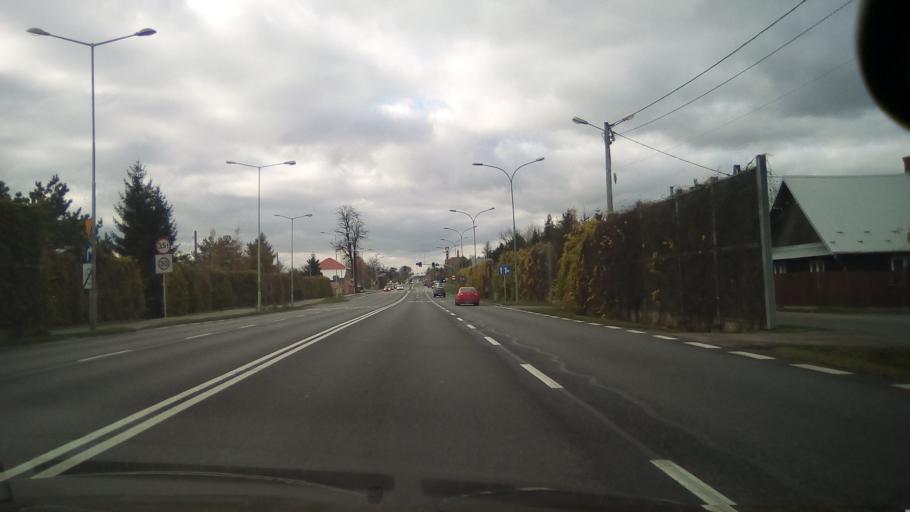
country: PL
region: Subcarpathian Voivodeship
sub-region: Powiat rzeszowski
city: Krasne
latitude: 50.0390
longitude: 22.0562
